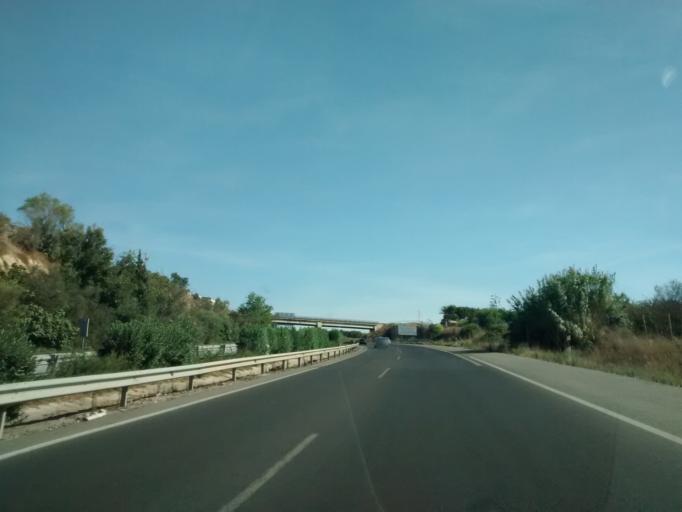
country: ES
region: Andalusia
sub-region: Provincia de Cadiz
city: Chiclana de la Frontera
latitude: 36.4217
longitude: -6.1152
